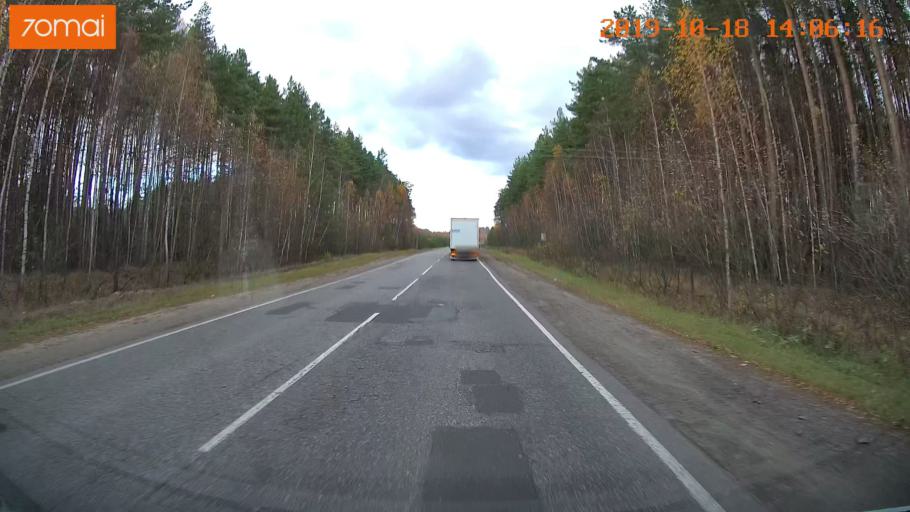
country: RU
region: Rjazan
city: Spas-Klepiki
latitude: 55.1432
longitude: 40.1495
